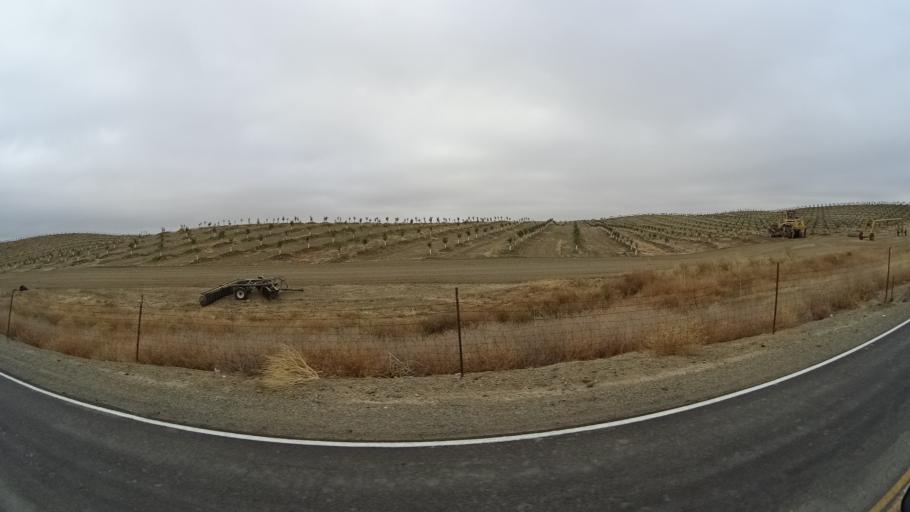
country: US
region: California
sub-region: Yolo County
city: Dunnigan
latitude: 38.8865
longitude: -122.0233
